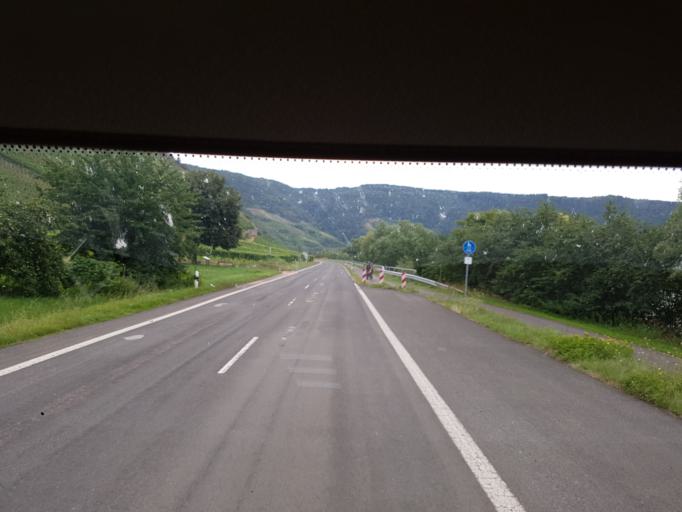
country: DE
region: Rheinland-Pfalz
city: Mesenich
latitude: 50.0926
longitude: 7.1994
